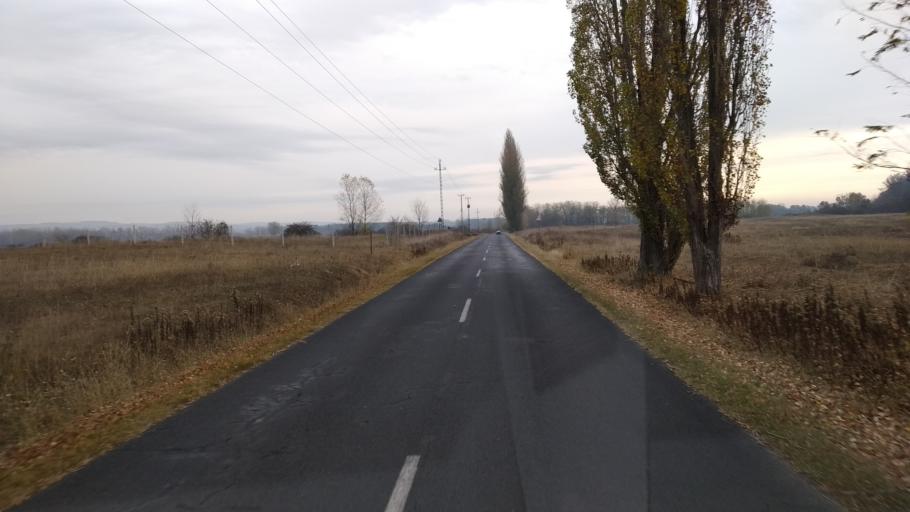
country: HU
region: Pest
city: Dunabogdany
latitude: 47.7921
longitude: 19.0759
